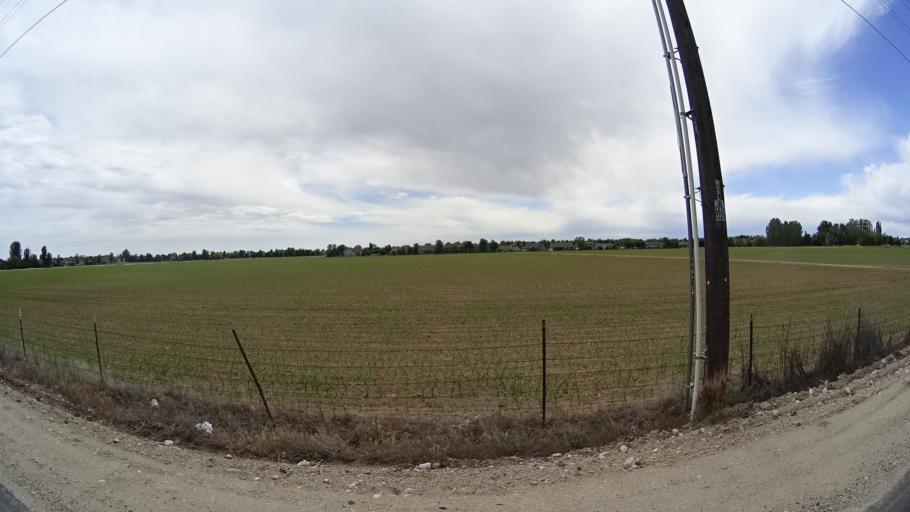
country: US
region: Idaho
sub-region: Ada County
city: Meridian
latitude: 43.5761
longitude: -116.3658
